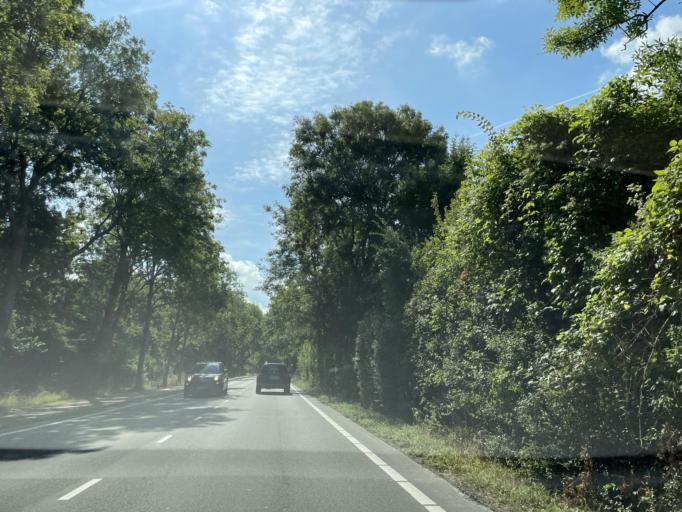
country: NL
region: Zeeland
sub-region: Gemeente Middelburg
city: Middelburg
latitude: 51.5040
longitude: 3.6031
